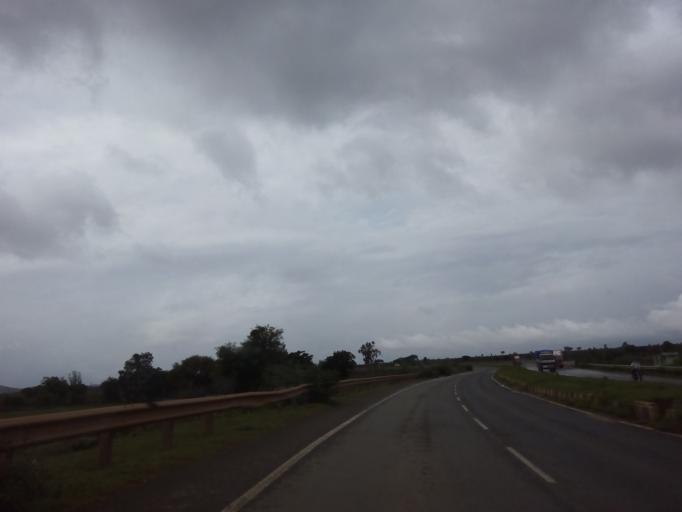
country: IN
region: Karnataka
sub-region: Haveri
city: Byadgi
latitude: 14.7332
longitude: 75.4663
